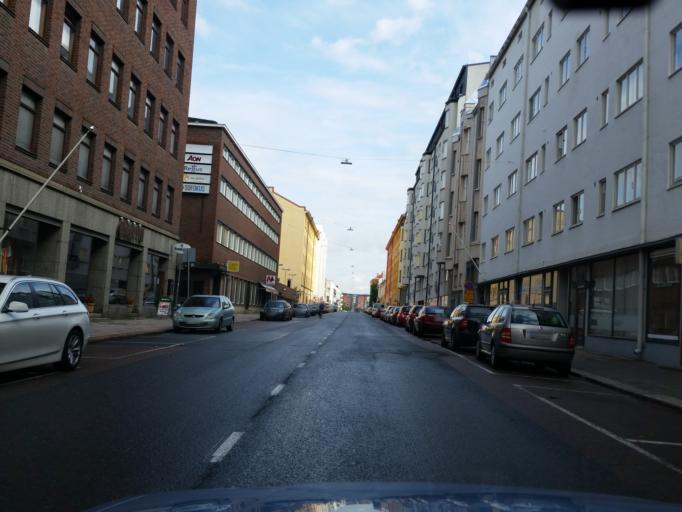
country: FI
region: Varsinais-Suomi
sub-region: Turku
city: Turku
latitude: 60.4537
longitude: 22.2568
